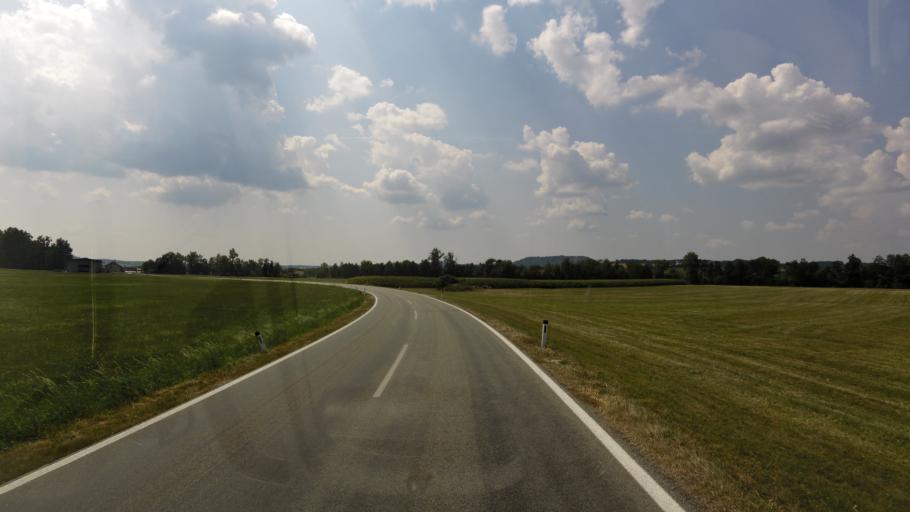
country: AT
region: Upper Austria
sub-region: Politischer Bezirk Ried im Innkreis
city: Waldzell
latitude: 48.1580
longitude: 13.4225
